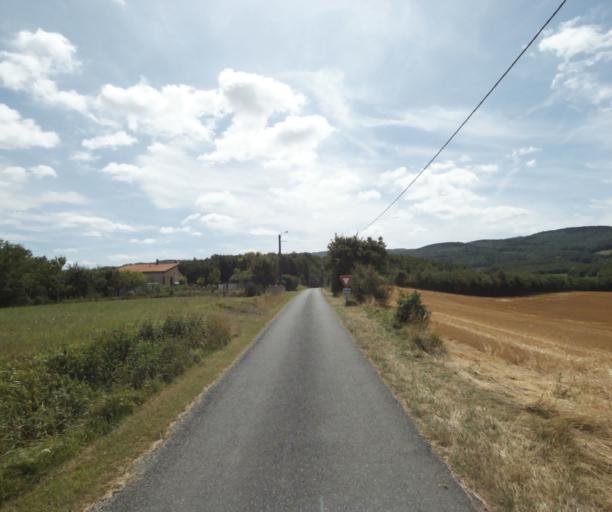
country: FR
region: Midi-Pyrenees
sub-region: Departement du Tarn
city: Dourgne
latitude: 43.4798
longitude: 2.1079
